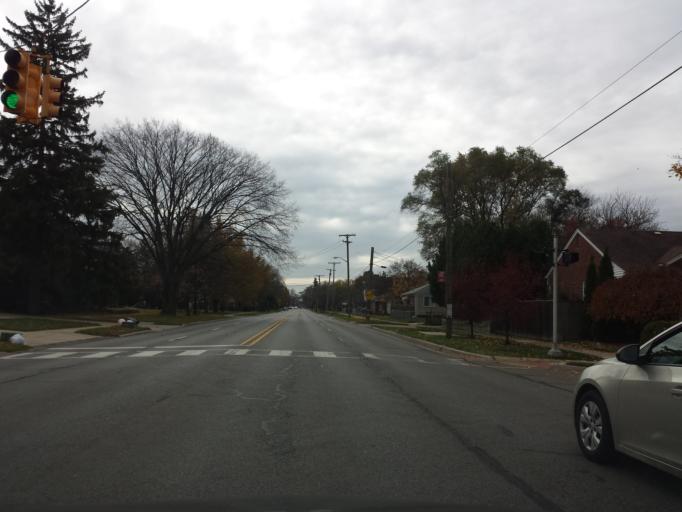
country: US
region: Michigan
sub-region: Oakland County
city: Clawson
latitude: 42.5264
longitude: -83.1459
